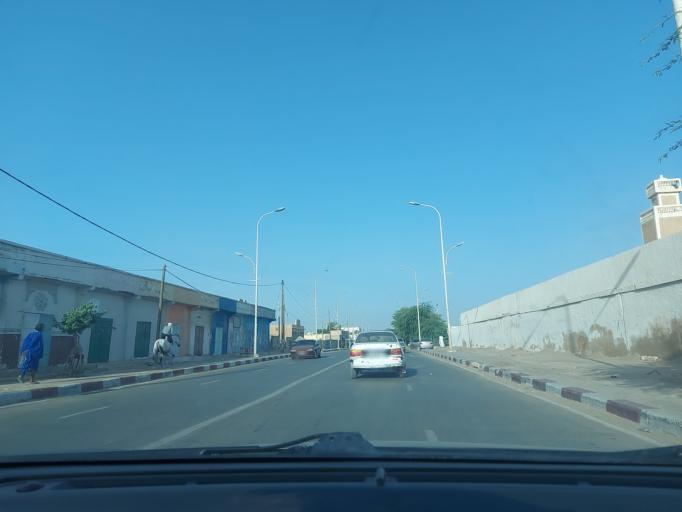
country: MR
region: Nouakchott
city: Nouakchott
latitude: 18.0861
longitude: -15.9885
